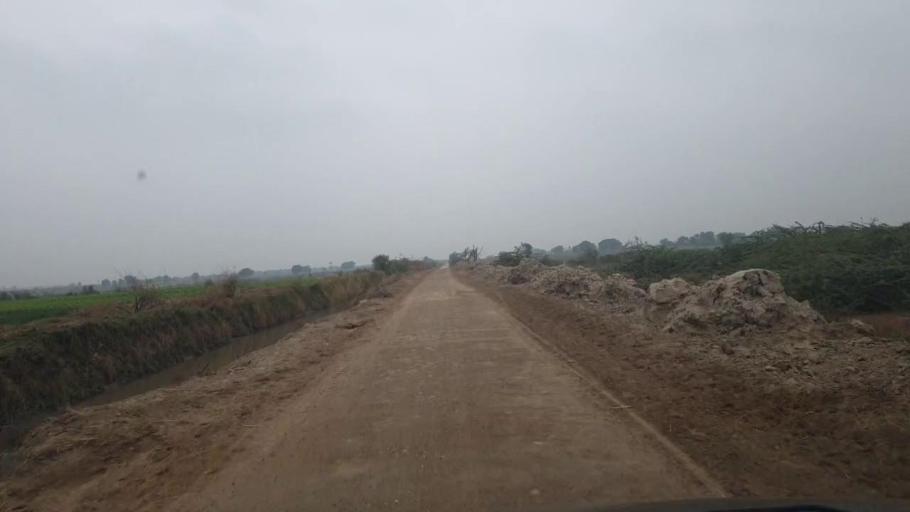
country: PK
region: Sindh
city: Tando Adam
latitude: 25.8433
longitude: 68.6824
